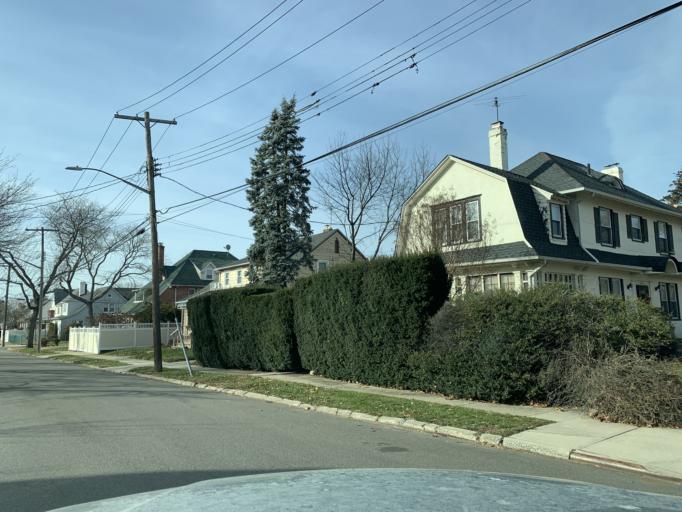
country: US
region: New York
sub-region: Queens County
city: Jamaica
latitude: 40.6941
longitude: -73.7696
